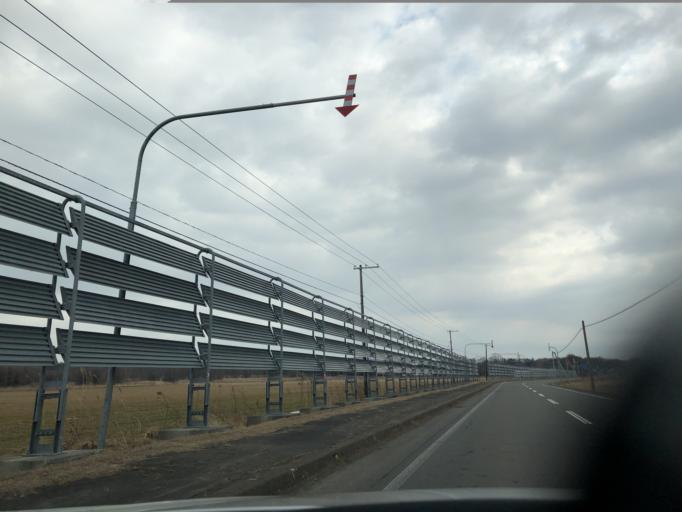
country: JP
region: Hokkaido
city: Chitose
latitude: 42.7619
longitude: 141.7665
